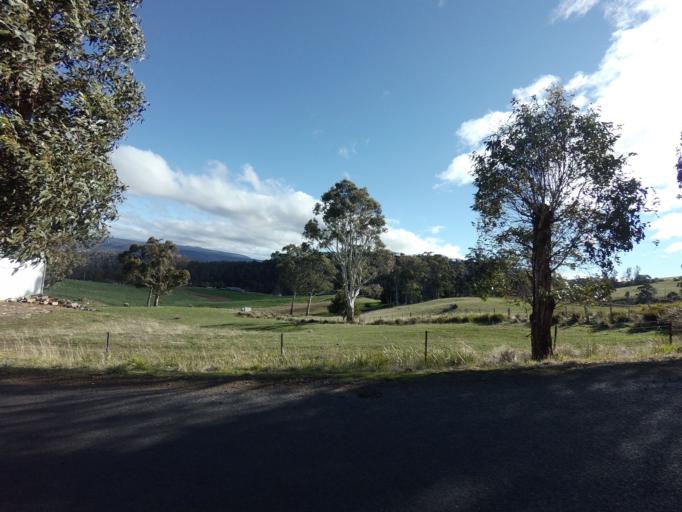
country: AU
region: Tasmania
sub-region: Derwent Valley
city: New Norfolk
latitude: -42.7207
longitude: 147.0326
